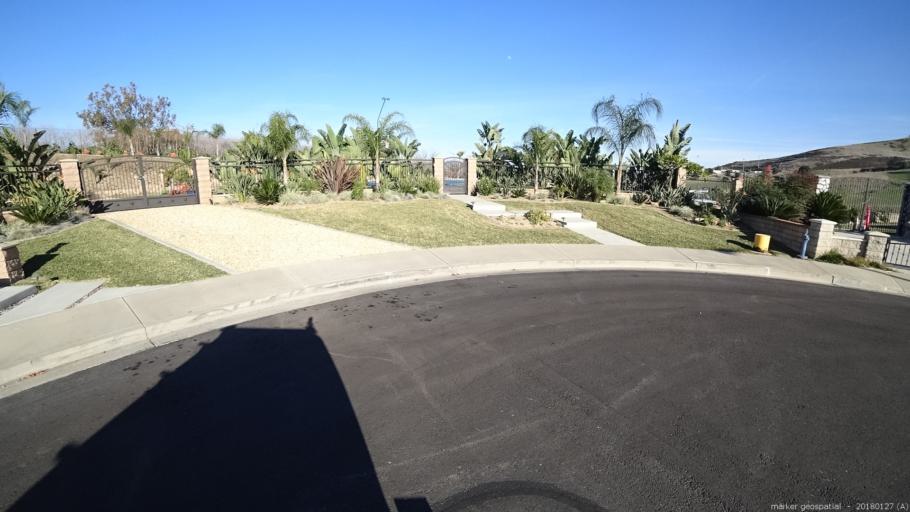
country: US
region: California
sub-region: Los Angeles County
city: Diamond Bar
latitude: 34.0236
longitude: -117.7877
